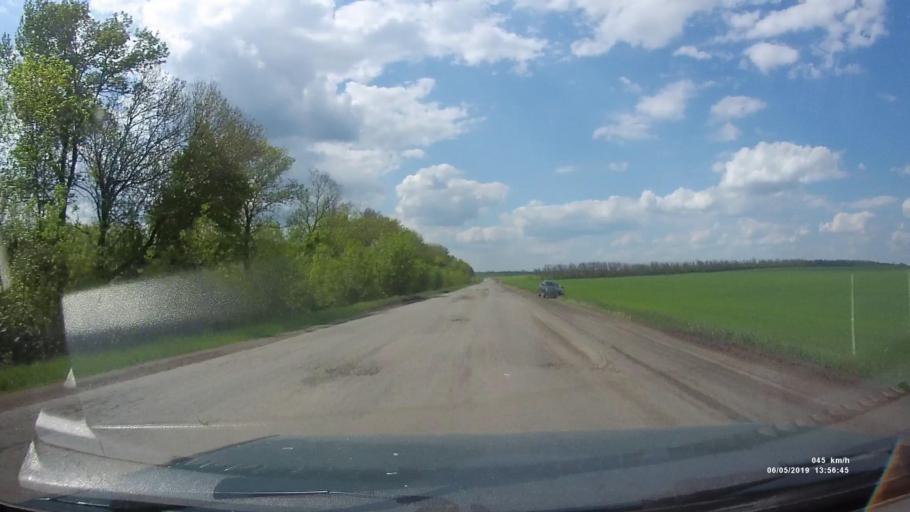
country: RU
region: Rostov
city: Melikhovskaya
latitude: 47.6822
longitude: 40.4284
